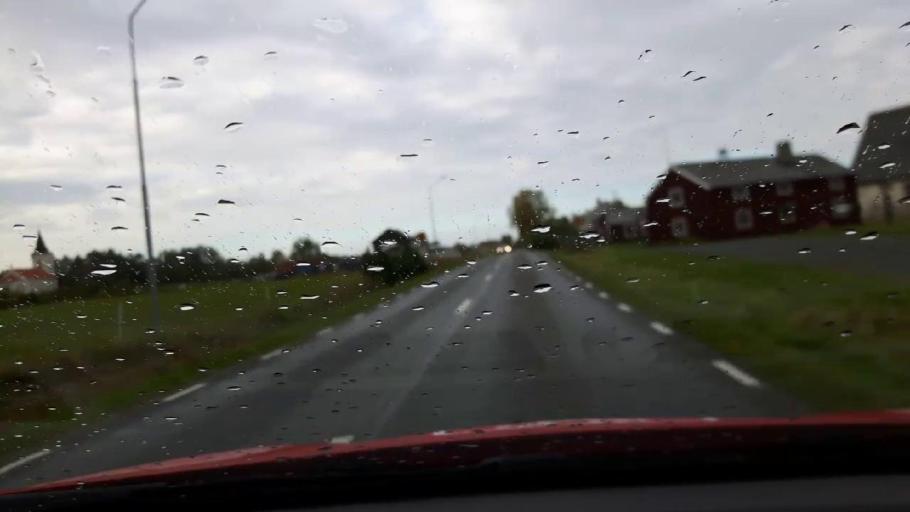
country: SE
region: Jaemtland
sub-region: Krokoms Kommun
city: Krokom
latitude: 63.1293
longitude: 14.2868
